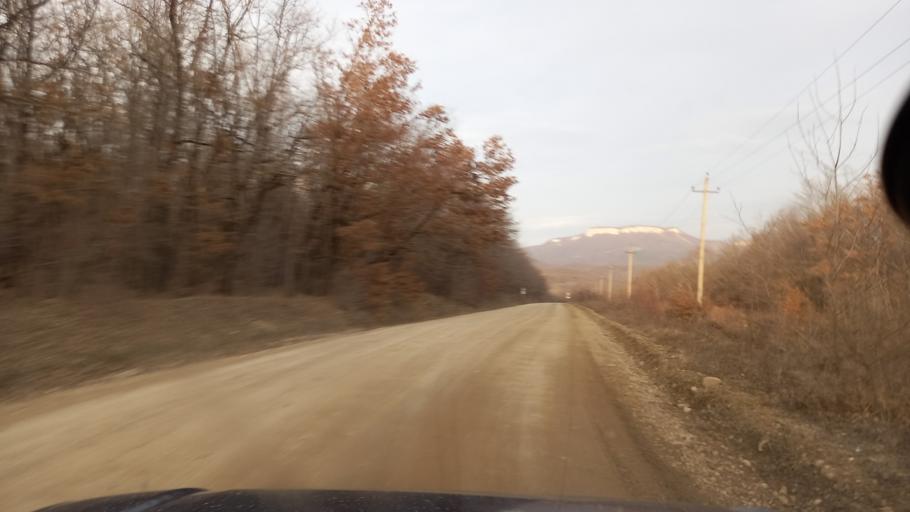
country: RU
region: Adygeya
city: Kamennomostskiy
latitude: 44.2054
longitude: 40.2495
